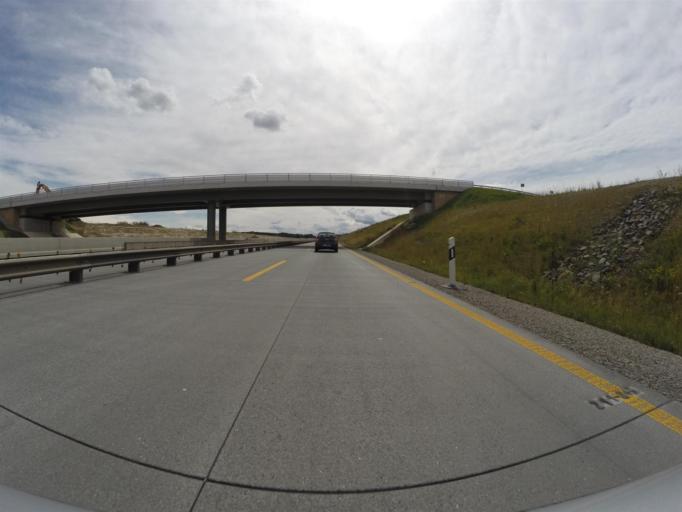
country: DE
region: Thuringia
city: Mossbach
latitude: 50.6823
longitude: 11.8305
